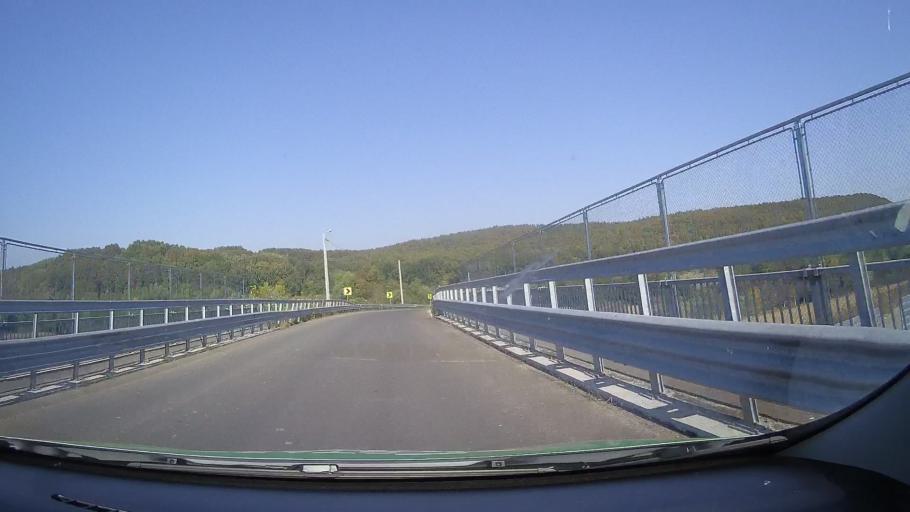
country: RO
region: Hunedoara
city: Lapugiu de Jos
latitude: 45.8893
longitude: 22.4804
